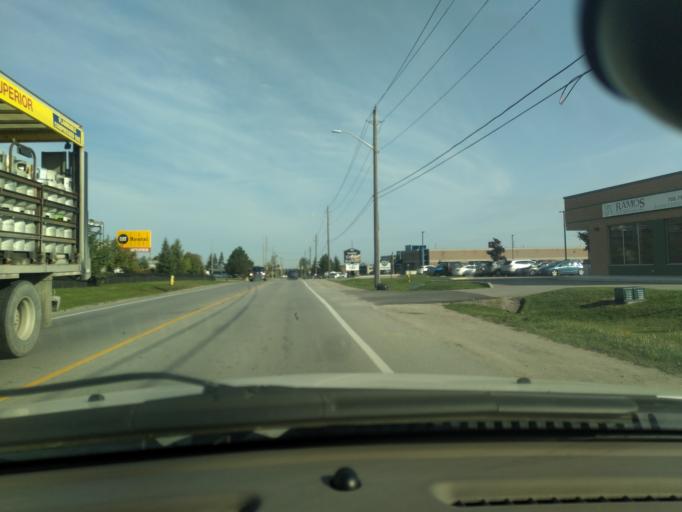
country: CA
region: Ontario
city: Barrie
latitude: 44.3503
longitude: -79.6643
